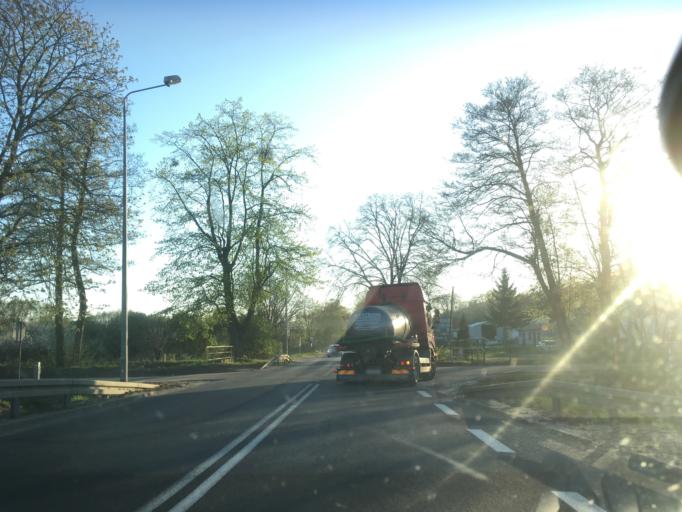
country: PL
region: Lubusz
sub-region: Powiat gorzowski
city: Jenin
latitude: 52.7125
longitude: 15.1535
